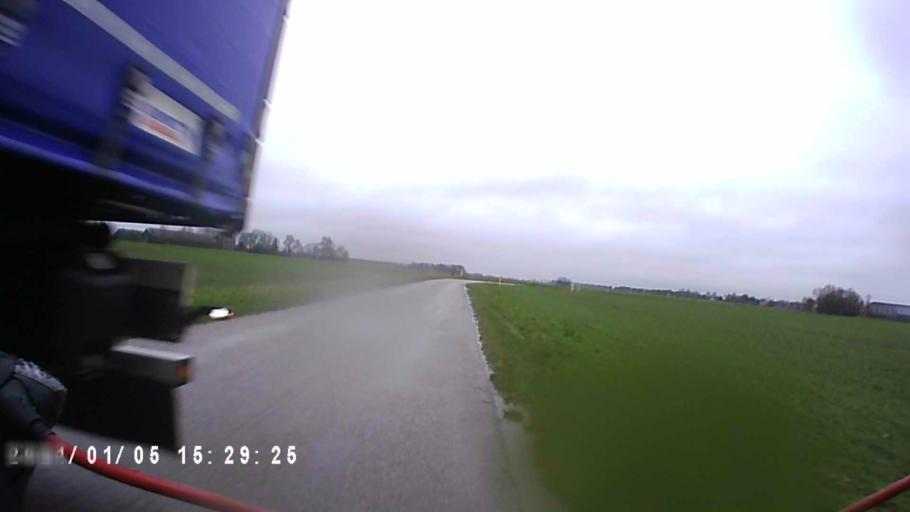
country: DE
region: Lower Saxony
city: Bunde
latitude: 53.2129
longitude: 7.1924
